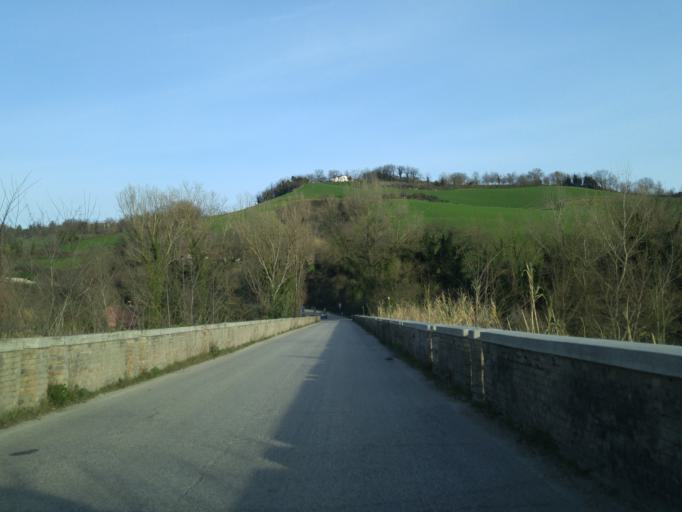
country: IT
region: The Marches
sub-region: Provincia di Pesaro e Urbino
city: Sant'Ippolito
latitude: 43.6869
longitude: 12.8599
